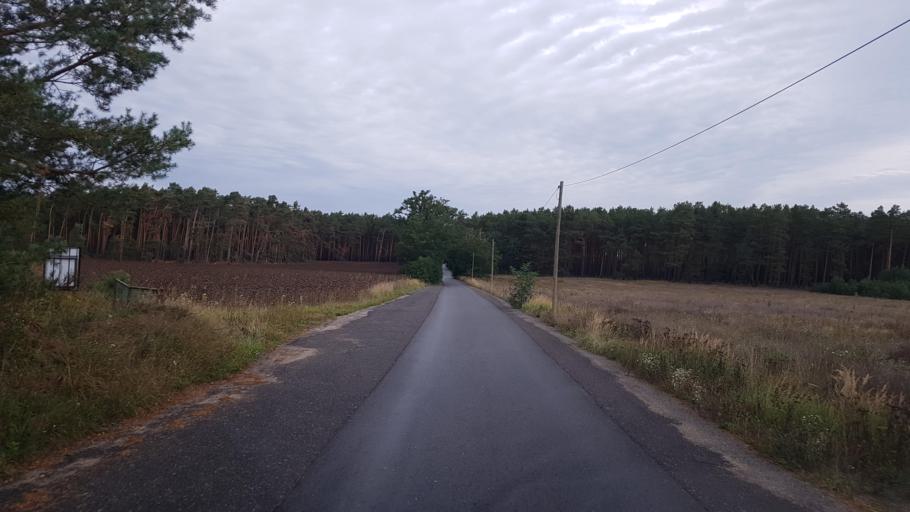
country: DE
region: Brandenburg
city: Kasel-Golzig
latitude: 51.9253
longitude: 13.7476
